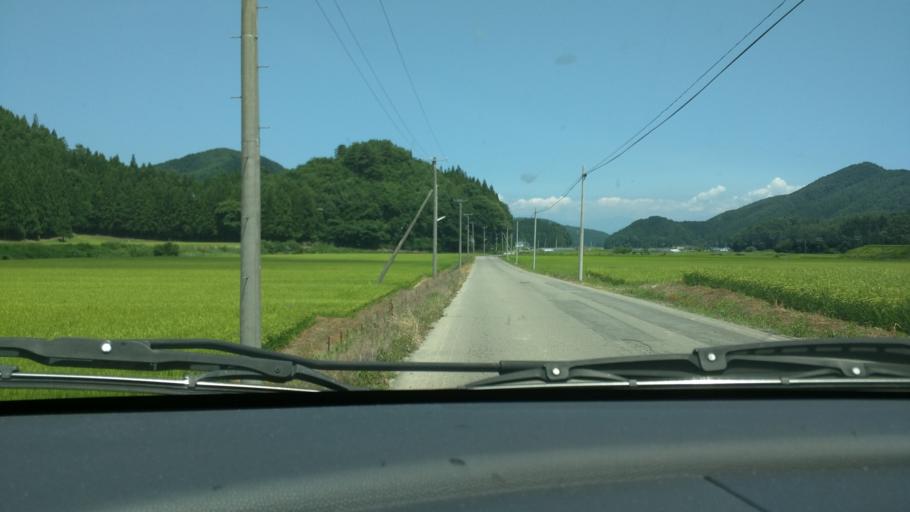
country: JP
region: Fukushima
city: Inawashiro
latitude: 37.3868
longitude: 140.0661
